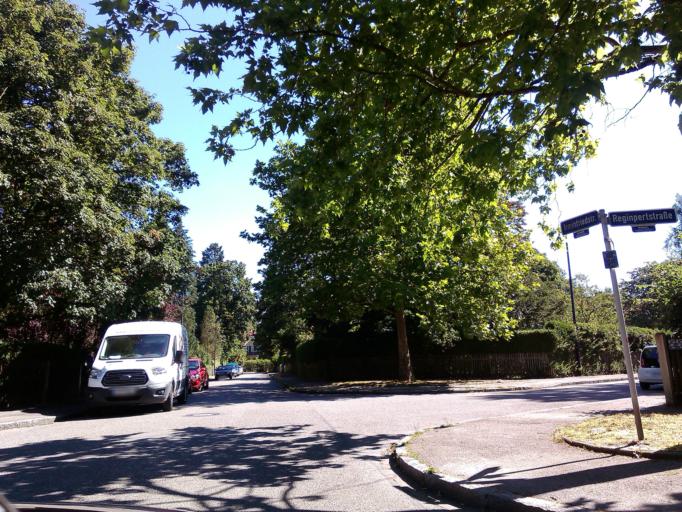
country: DE
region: Bavaria
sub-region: Upper Bavaria
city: Grafelfing
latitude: 48.1202
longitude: 11.4227
